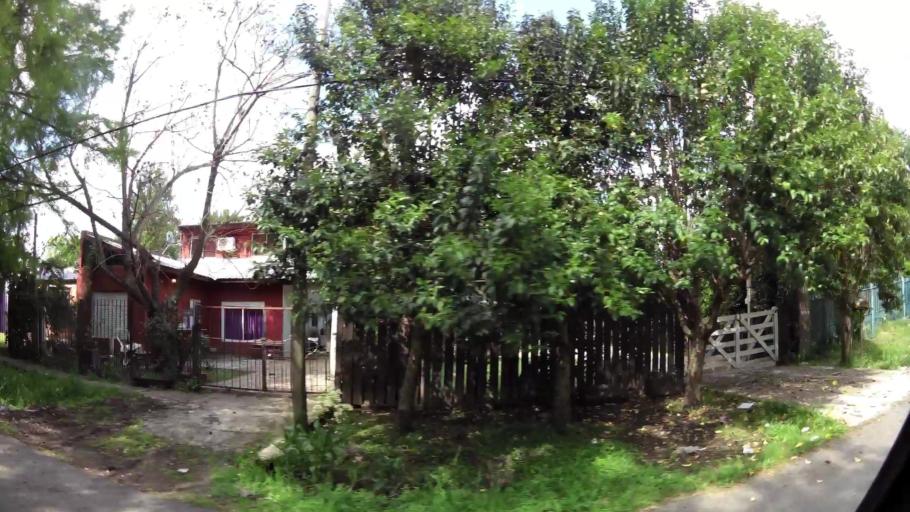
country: AR
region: Buenos Aires
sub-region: Partido de Quilmes
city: Quilmes
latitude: -34.8363
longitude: -58.1704
